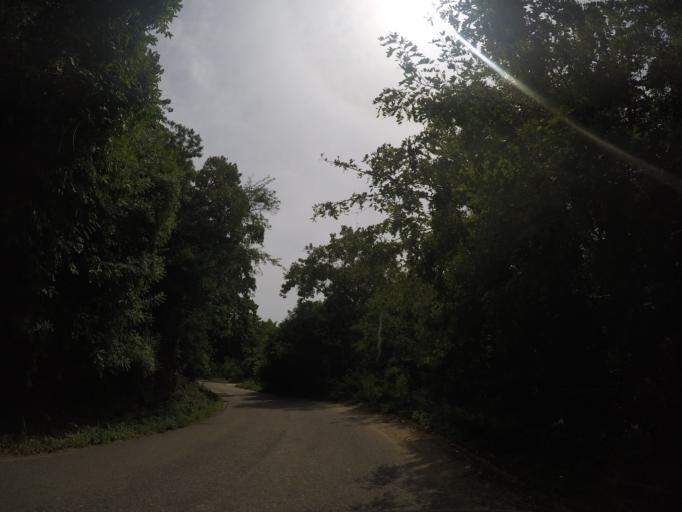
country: MX
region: Oaxaca
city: Santa Maria Tonameca
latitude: 15.6676
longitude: -96.5343
